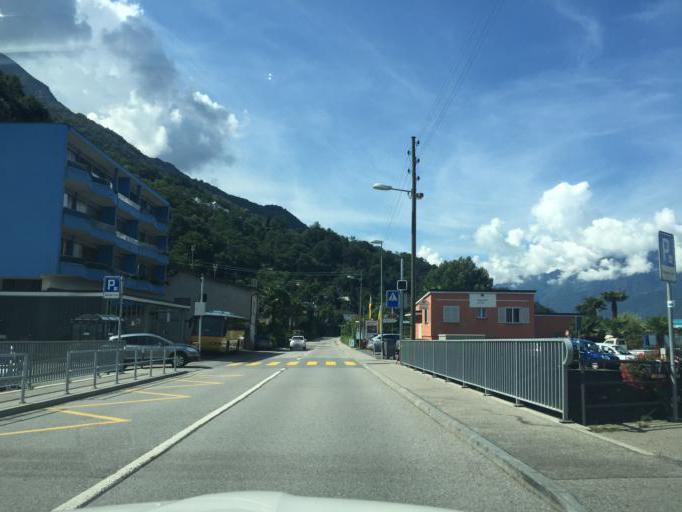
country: CH
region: Ticino
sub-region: Locarno District
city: Magadino
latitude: 46.1431
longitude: 8.8399
